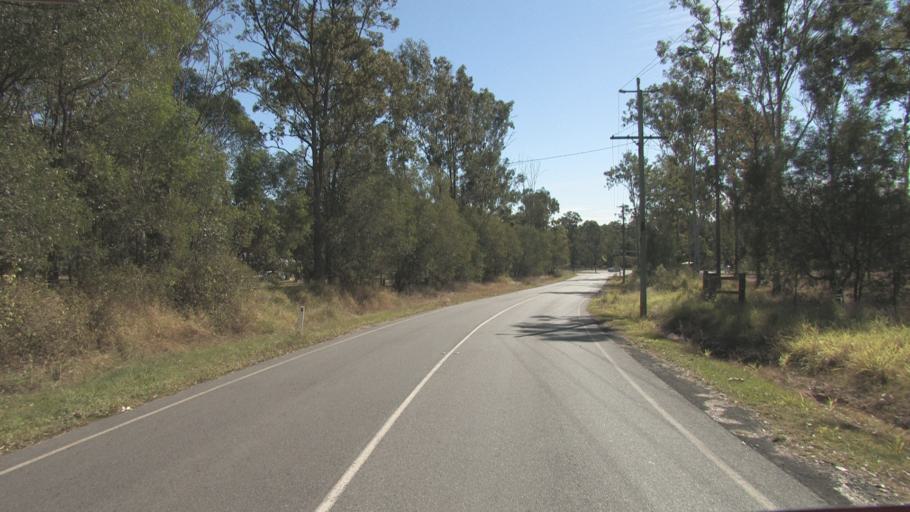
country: AU
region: Queensland
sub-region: Logan
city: North Maclean
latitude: -27.8189
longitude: 152.9714
